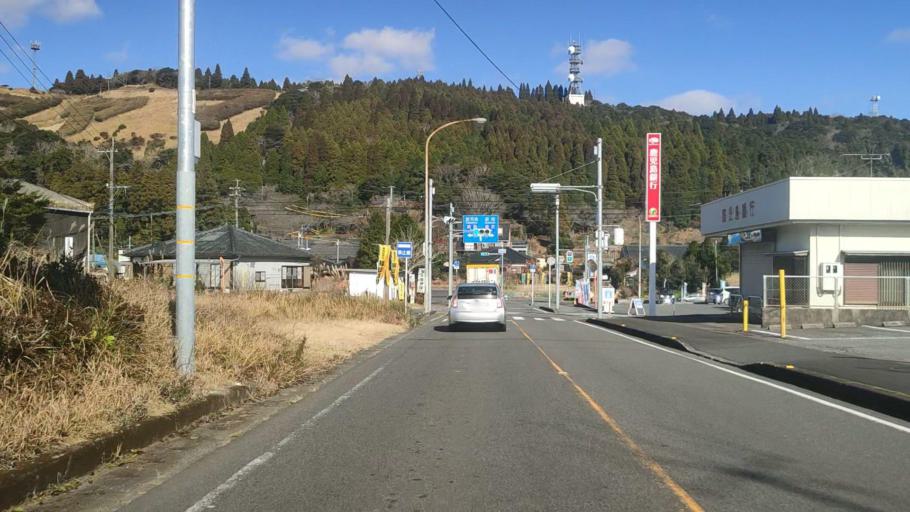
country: JP
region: Kagoshima
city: Kokubu-matsuki
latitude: 31.6718
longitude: 130.8457
